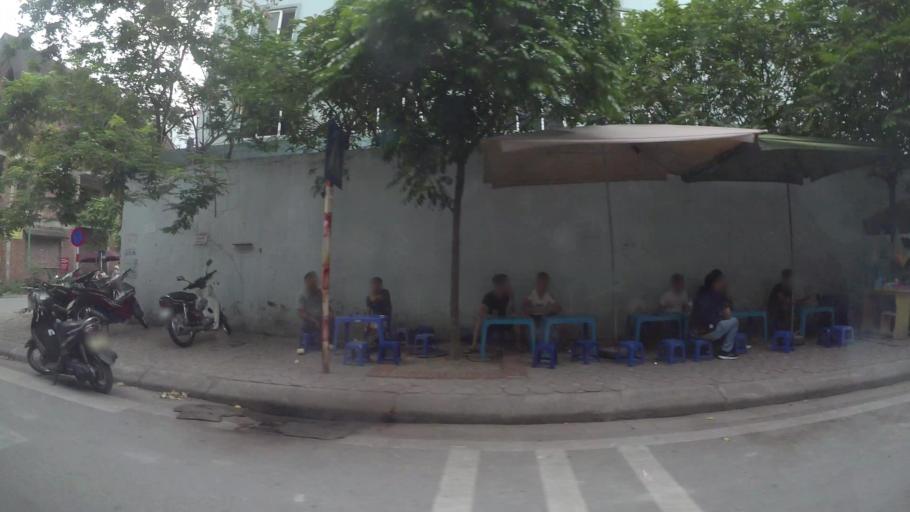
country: VN
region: Ha Noi
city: Cau Dien
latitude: 21.0316
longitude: 105.7617
